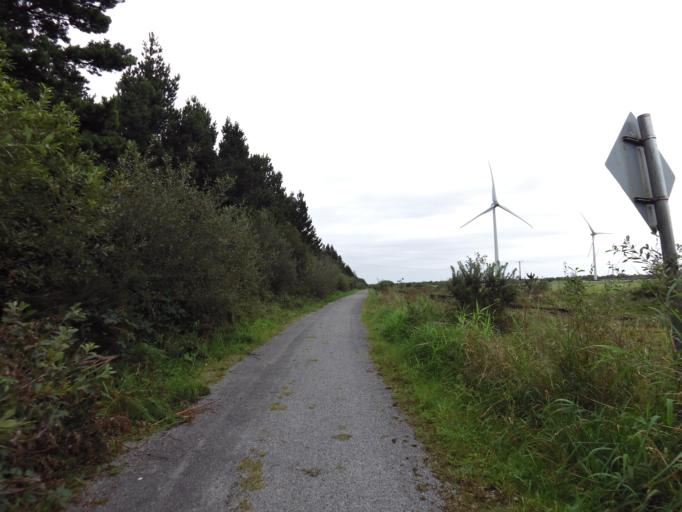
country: IE
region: Leinster
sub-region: Uibh Fhaili
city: Ferbane
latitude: 53.2311
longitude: -7.7736
